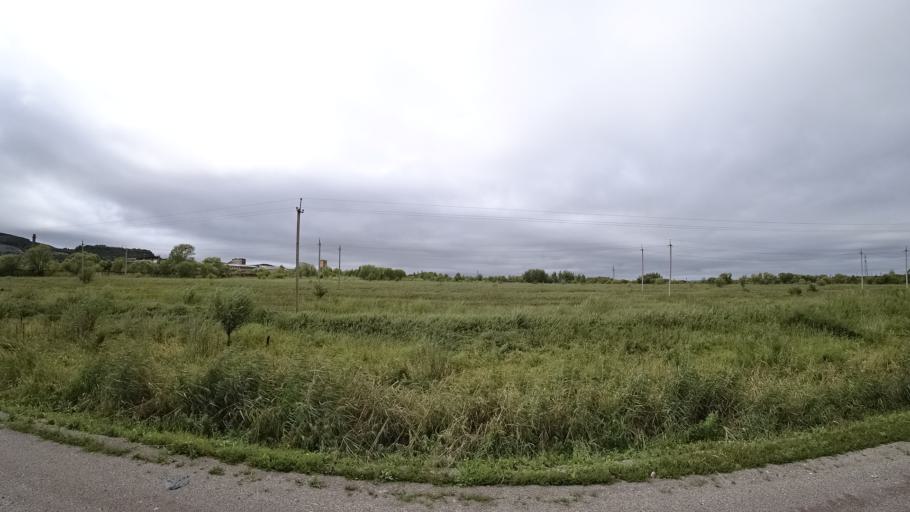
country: RU
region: Primorskiy
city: Monastyrishche
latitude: 44.1724
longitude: 132.4412
